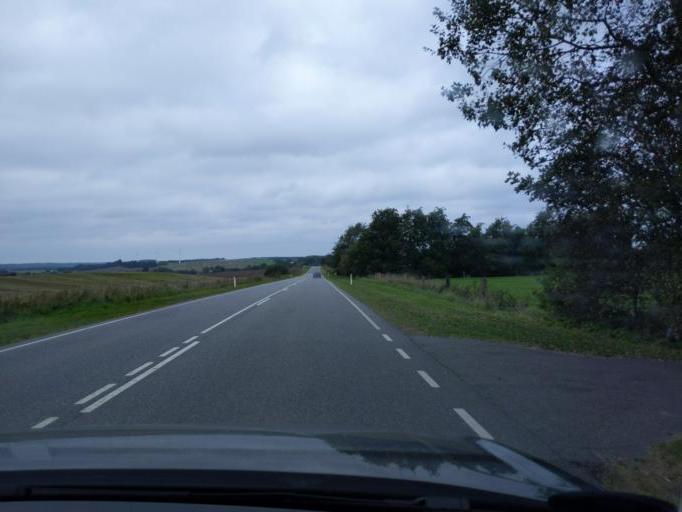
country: DK
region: North Denmark
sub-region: Mariagerfjord Kommune
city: Hobro
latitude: 56.5629
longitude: 9.8396
